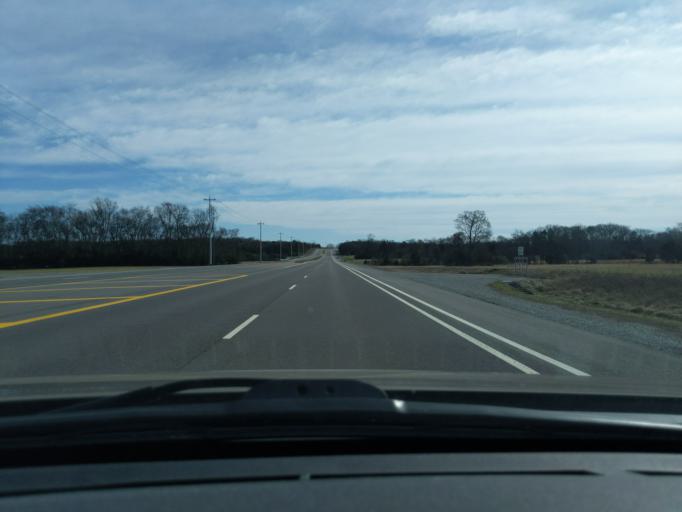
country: US
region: Tennessee
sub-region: Wilson County
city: Mount Juliet
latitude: 36.1996
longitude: -86.4919
